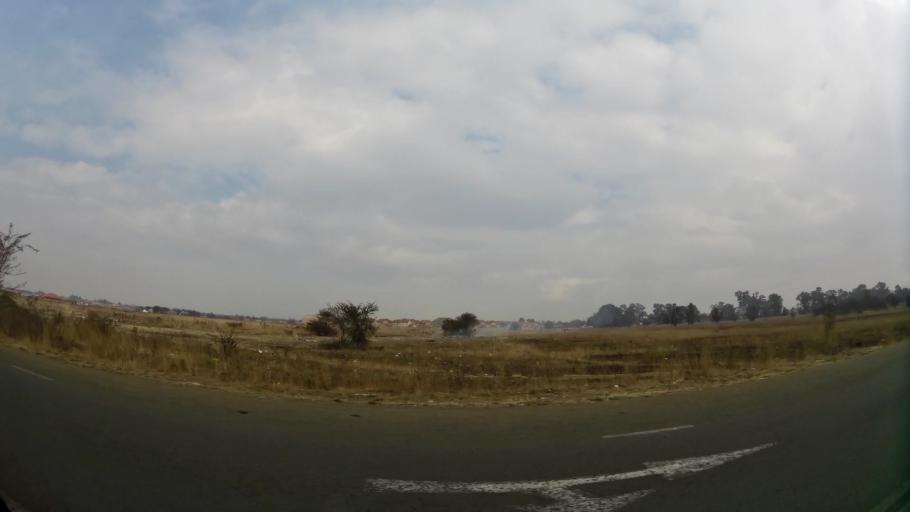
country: ZA
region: Gauteng
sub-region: Sedibeng District Municipality
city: Vanderbijlpark
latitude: -26.6767
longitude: 27.8433
